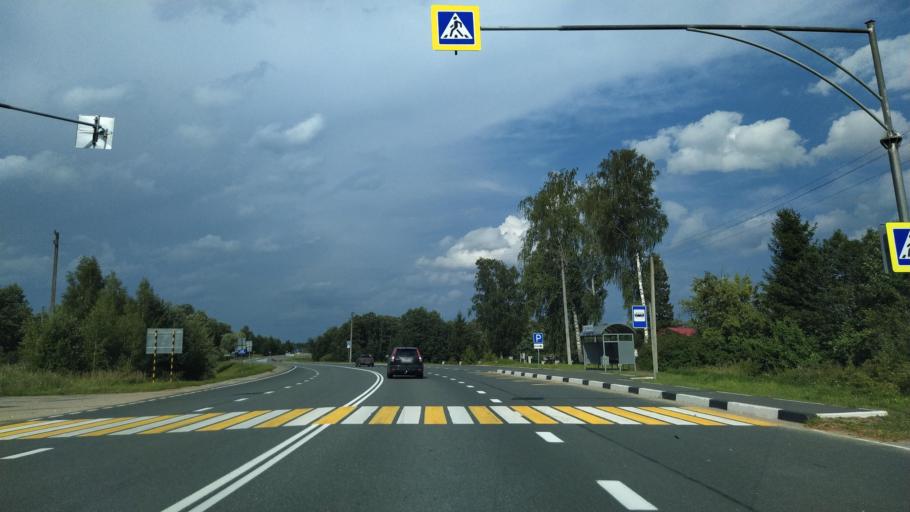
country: RU
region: Pskov
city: Porkhov
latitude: 57.8501
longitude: 29.5500
